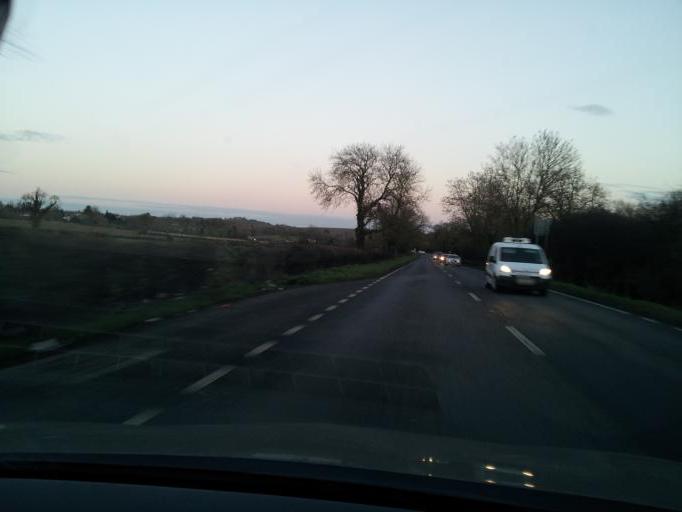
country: GB
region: England
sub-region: District of Rutland
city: Ridlington
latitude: 52.5964
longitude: -0.8093
